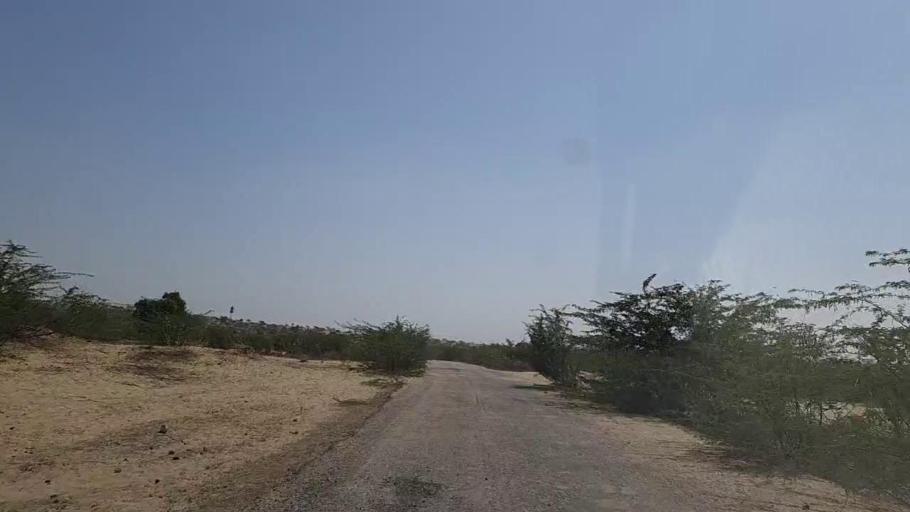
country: PK
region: Sindh
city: Diplo
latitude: 24.4945
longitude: 69.4333
